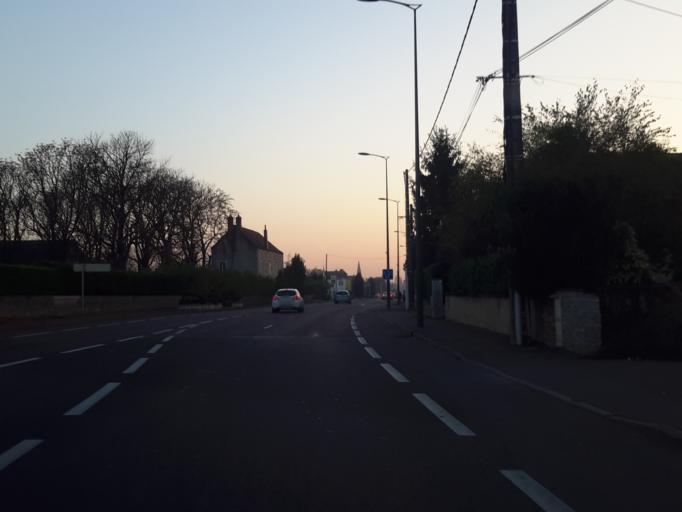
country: FR
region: Bourgogne
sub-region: Departement de la Cote-d'Or
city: Beaune
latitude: 47.0377
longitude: 4.8474
